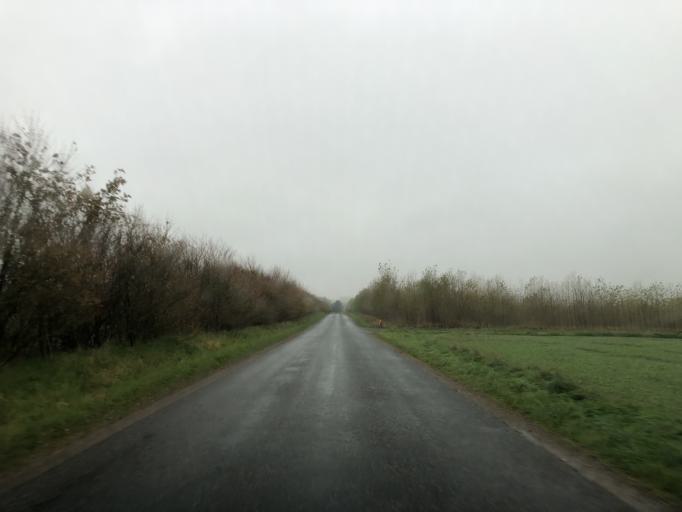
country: DK
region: Central Jutland
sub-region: Herning Kommune
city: Snejbjerg
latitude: 56.0816
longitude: 8.9132
